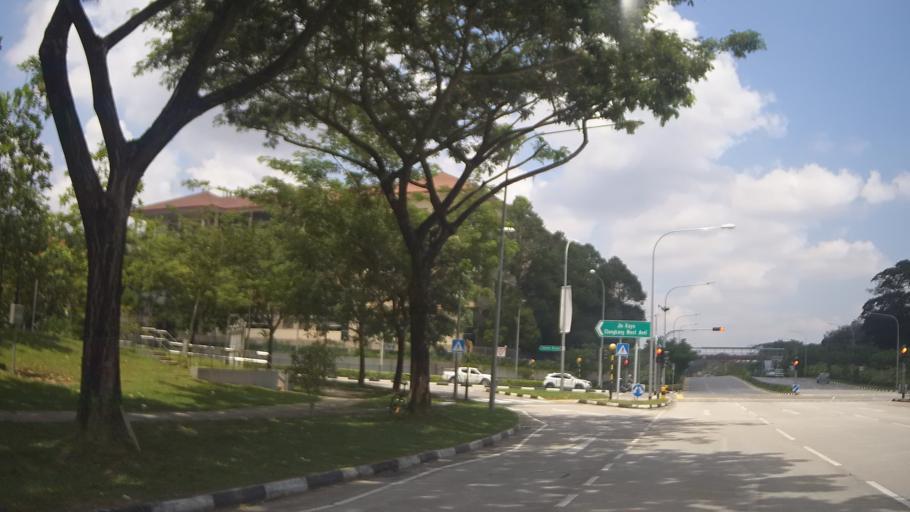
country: MY
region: Johor
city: Kampung Pasir Gudang Baru
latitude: 1.3949
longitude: 103.8734
